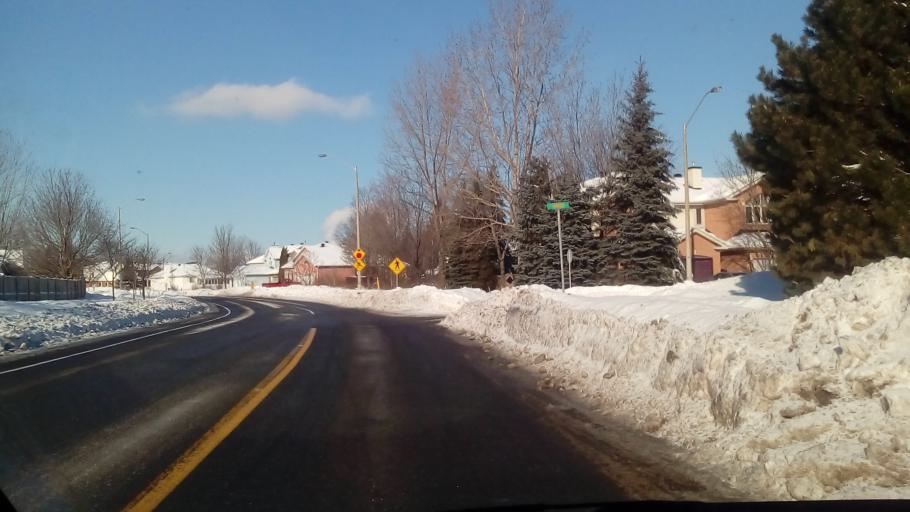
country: CA
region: Ontario
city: Ottawa
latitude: 45.4306
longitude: -75.6242
